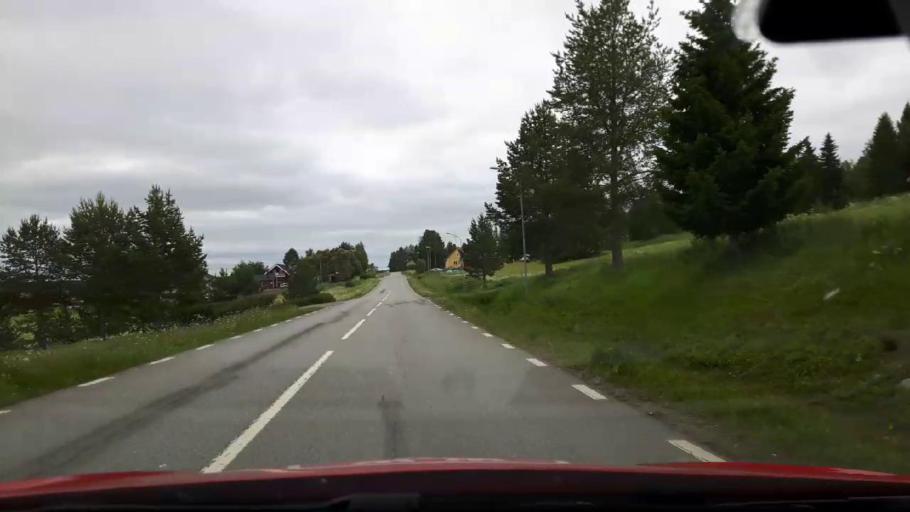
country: SE
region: Jaemtland
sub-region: Stroemsunds Kommun
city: Stroemsund
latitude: 63.5646
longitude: 15.3948
